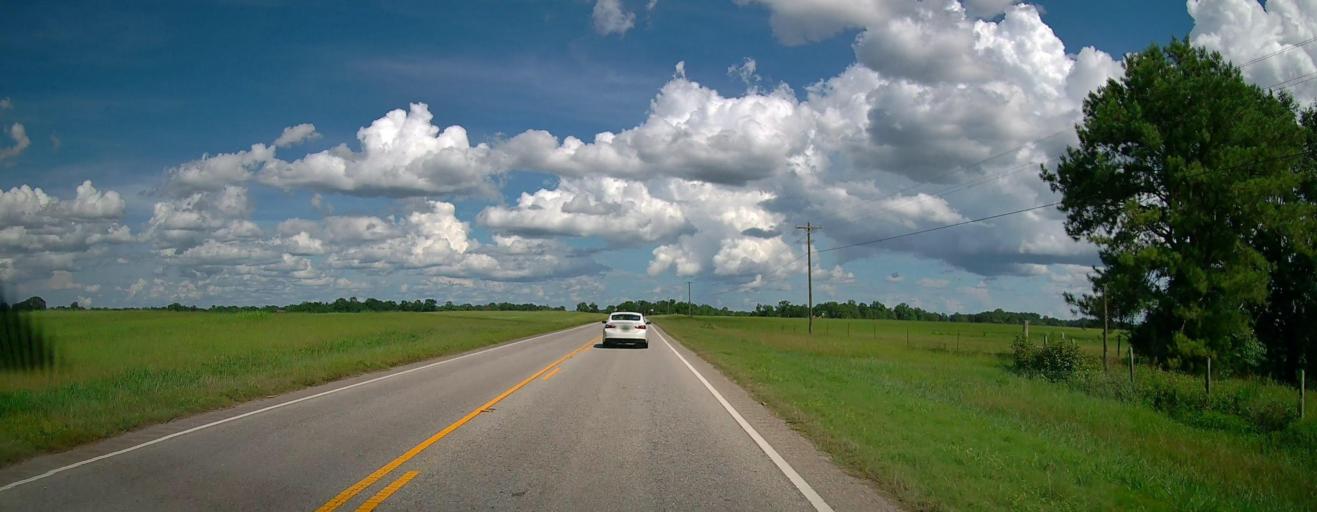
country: US
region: Alabama
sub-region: Lee County
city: Auburn
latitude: 32.4289
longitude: -85.4609
